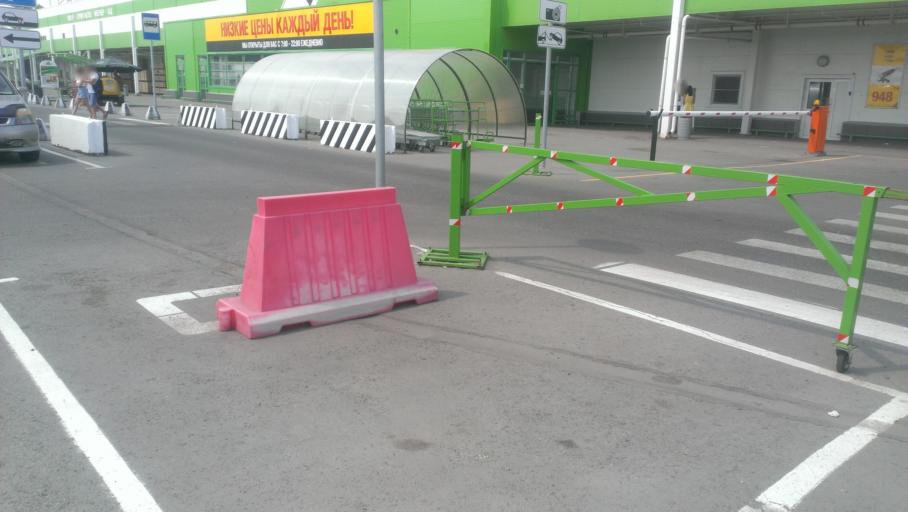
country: RU
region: Altai Krai
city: Novosilikatnyy
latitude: 53.3494
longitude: 83.6332
